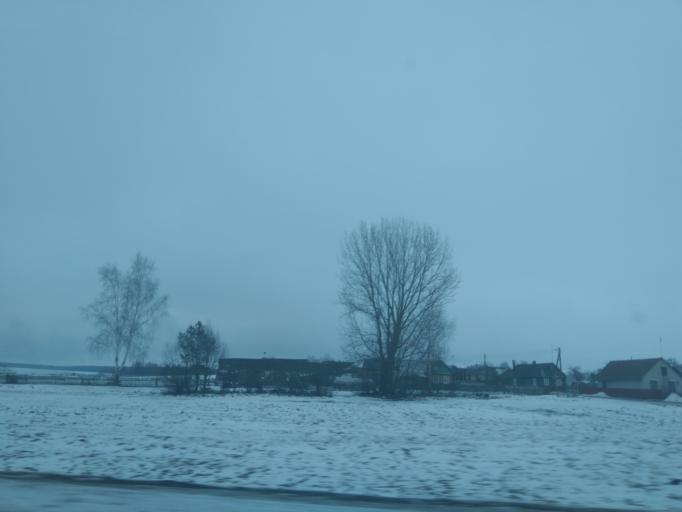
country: BY
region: Minsk
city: Haradzyeya
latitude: 53.3008
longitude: 26.5754
